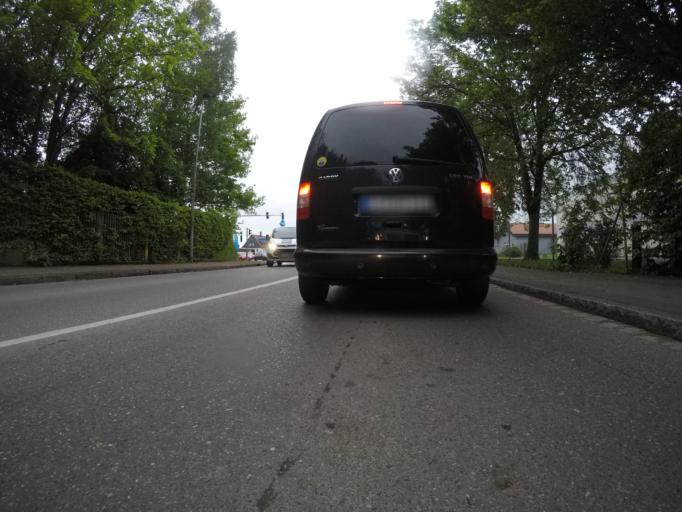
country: DE
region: Baden-Wuerttemberg
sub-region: Regierungsbezirk Stuttgart
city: Weilheim an der Teck
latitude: 48.6197
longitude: 9.5398
